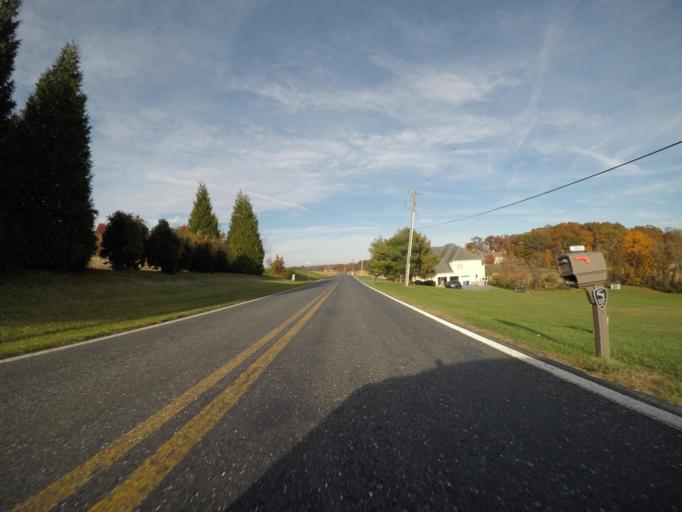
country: US
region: Maryland
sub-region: Carroll County
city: Hampstead
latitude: 39.5640
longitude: -76.9064
